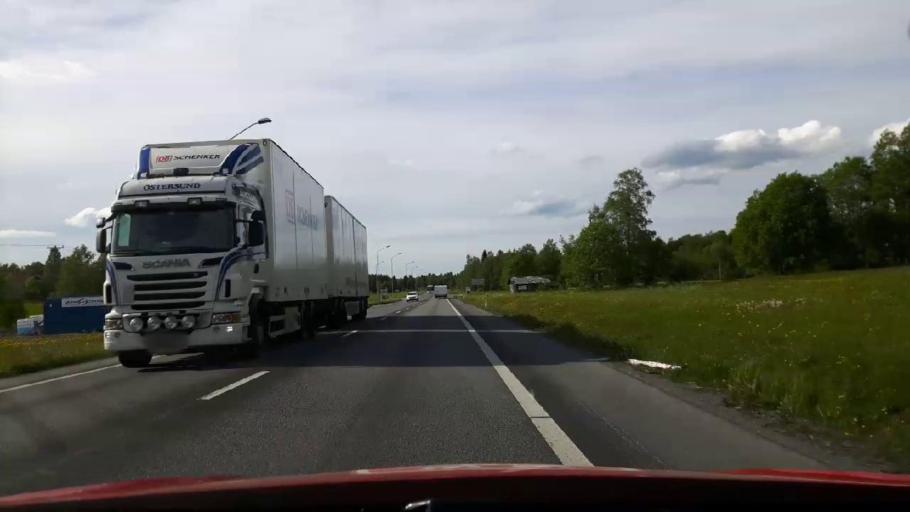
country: SE
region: Jaemtland
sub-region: OEstersunds Kommun
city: Brunflo
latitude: 63.1098
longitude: 14.7967
